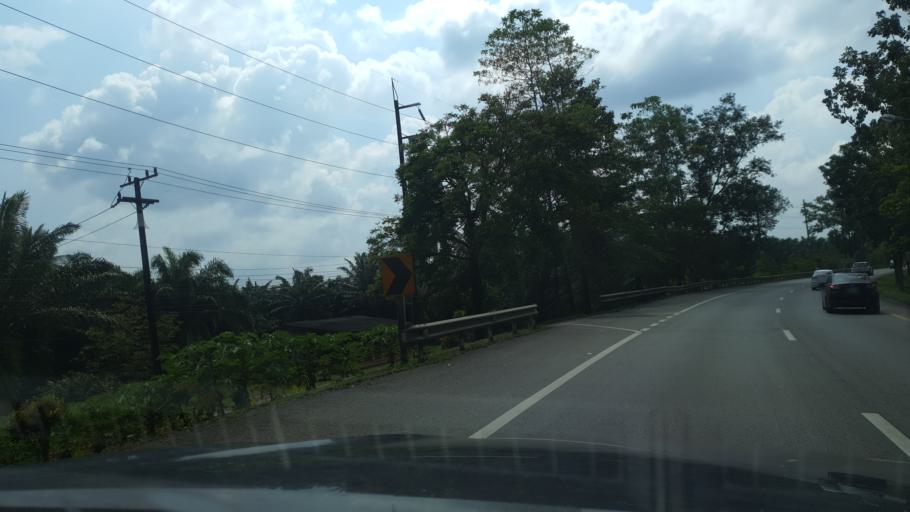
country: TH
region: Chumphon
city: Chumphon
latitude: 10.5481
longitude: 99.1186
